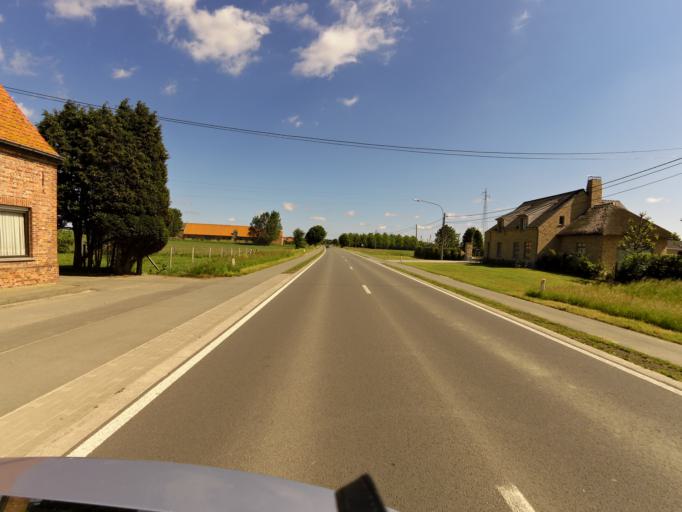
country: BE
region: Flanders
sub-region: Provincie West-Vlaanderen
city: Diksmuide
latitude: 50.9669
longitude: 2.8686
